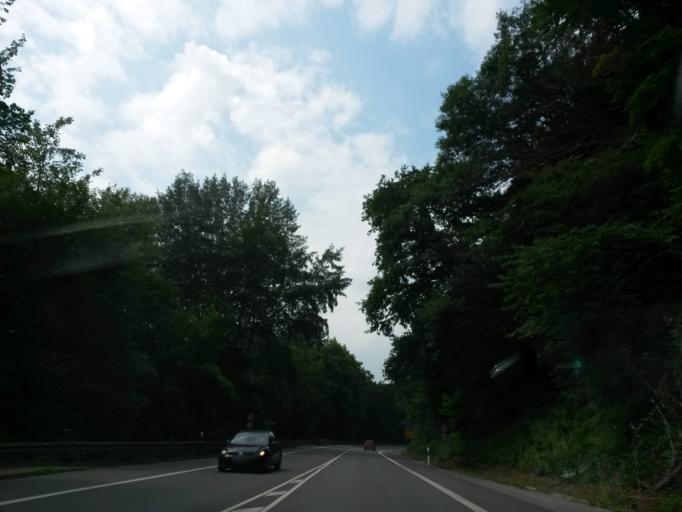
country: DE
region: North Rhine-Westphalia
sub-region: Regierungsbezirk Arnsberg
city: Hagen
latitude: 51.3815
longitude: 7.5365
